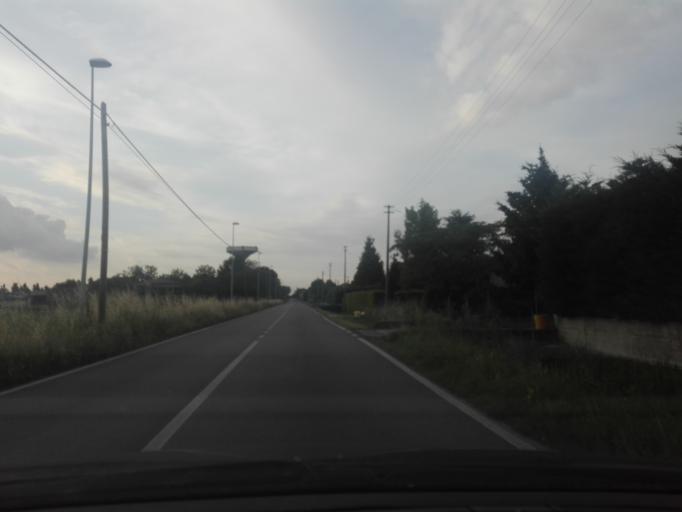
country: IT
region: Veneto
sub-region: Provincia di Rovigo
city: Villadose
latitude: 45.0616
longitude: 11.9031
